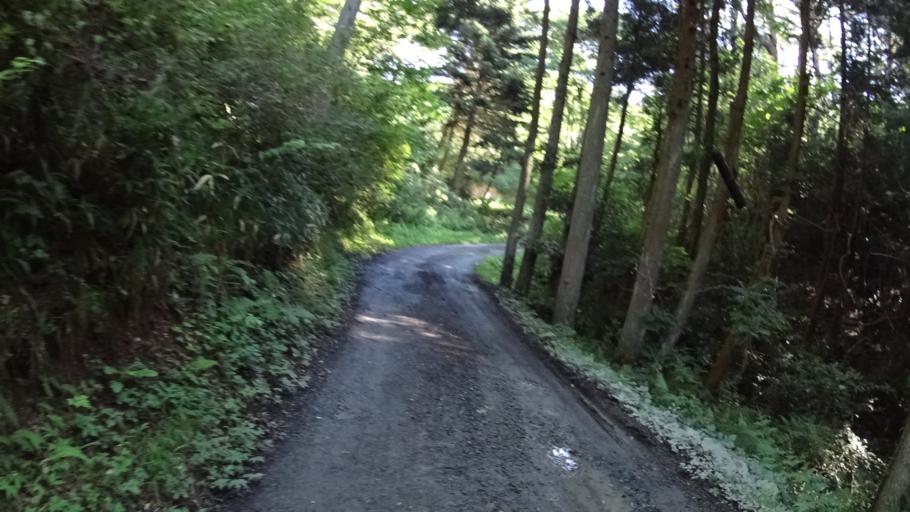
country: JP
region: Iwate
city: Ofunato
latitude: 38.8726
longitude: 141.6263
